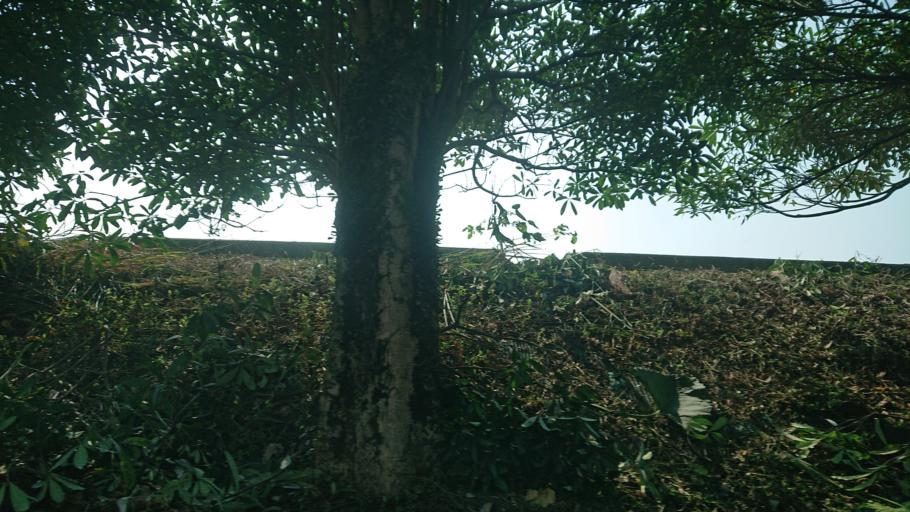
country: TW
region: Taiwan
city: Lugu
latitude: 23.7304
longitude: 120.6653
